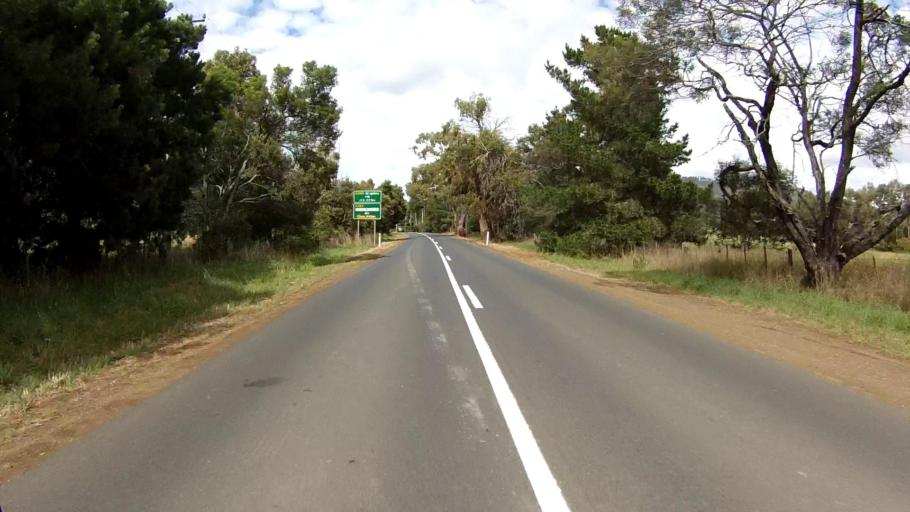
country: AU
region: Tasmania
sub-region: Clarence
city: Cambridge
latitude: -42.7618
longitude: 147.3972
